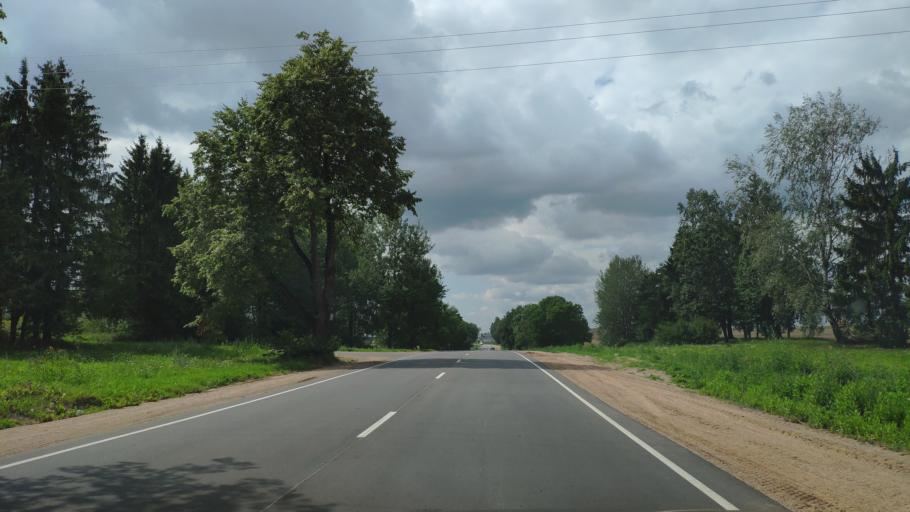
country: BY
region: Minsk
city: Zaslawye
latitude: 54.0067
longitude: 27.3279
